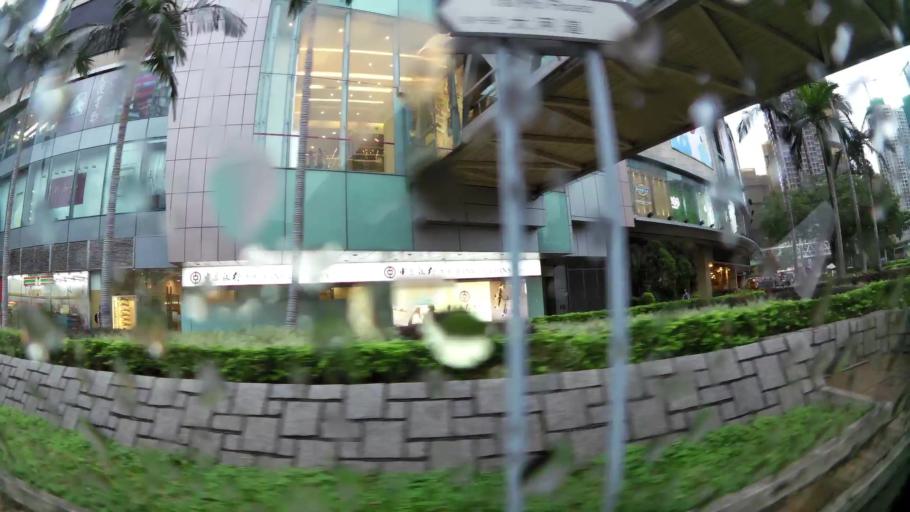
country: HK
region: Tsuen Wan
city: Tsuen Wan
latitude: 22.3707
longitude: 114.1141
